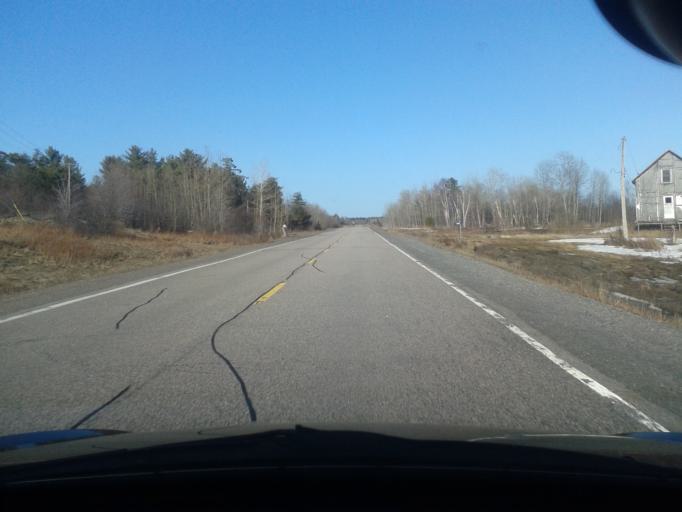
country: CA
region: Ontario
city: Greater Sudbury
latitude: 46.2737
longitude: -80.2864
